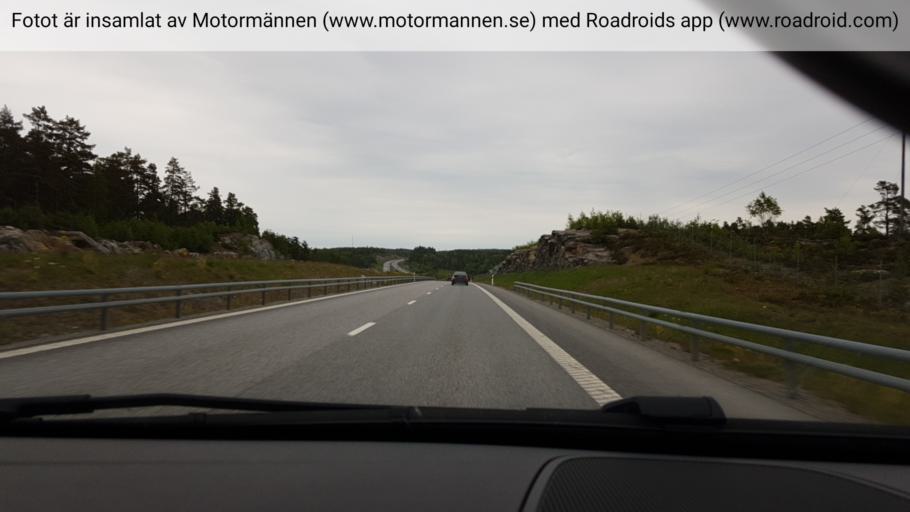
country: SE
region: Stockholm
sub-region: Nynashamns Kommun
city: Osmo
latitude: 59.0498
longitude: 17.9926
